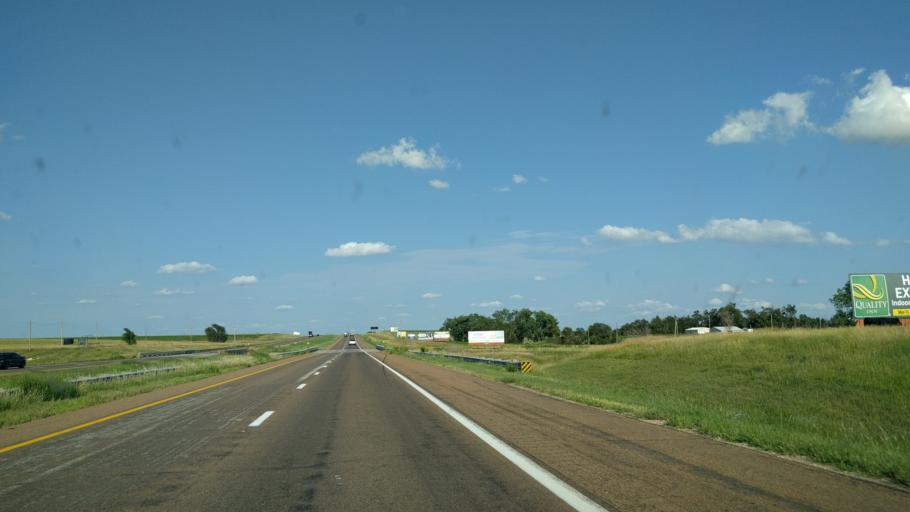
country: US
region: Kansas
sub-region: Ellis County
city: Hays
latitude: 38.9215
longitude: -99.4150
